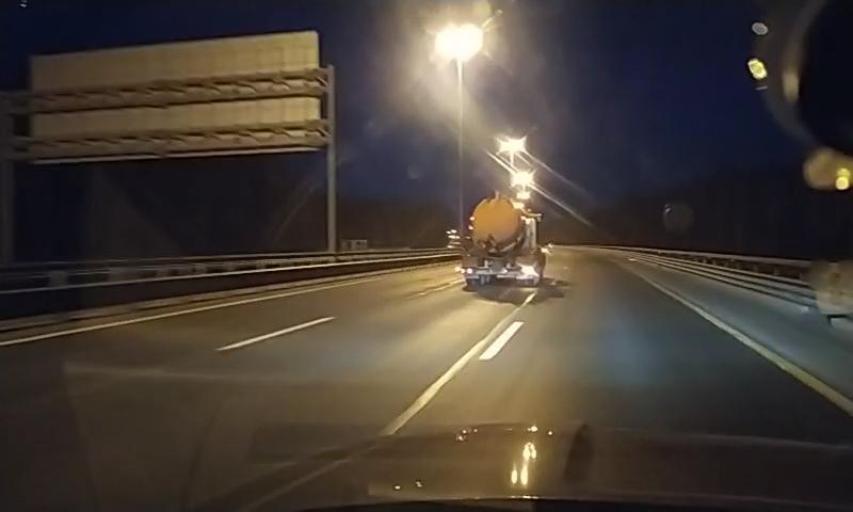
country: RU
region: St.-Petersburg
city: Pesochnyy
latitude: 60.0759
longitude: 30.1293
